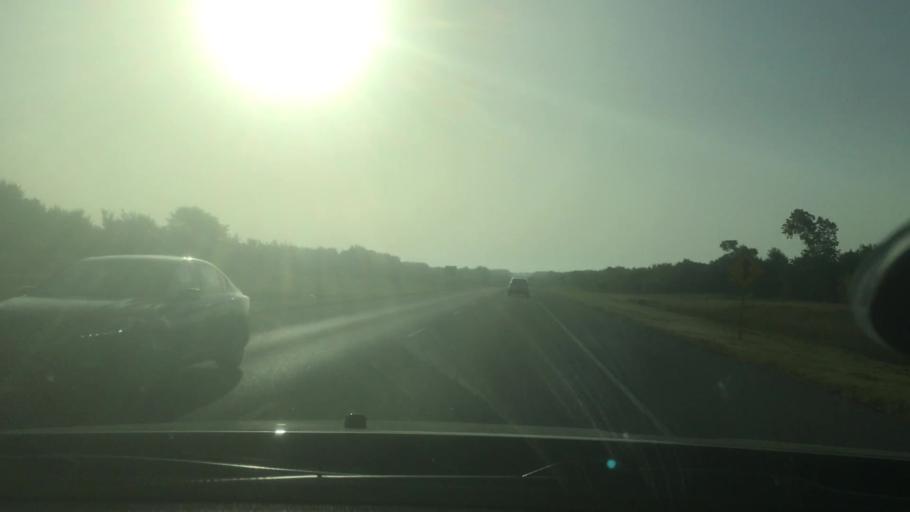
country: US
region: Oklahoma
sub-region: Pontotoc County
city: Ada
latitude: 34.6422
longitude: -96.5268
